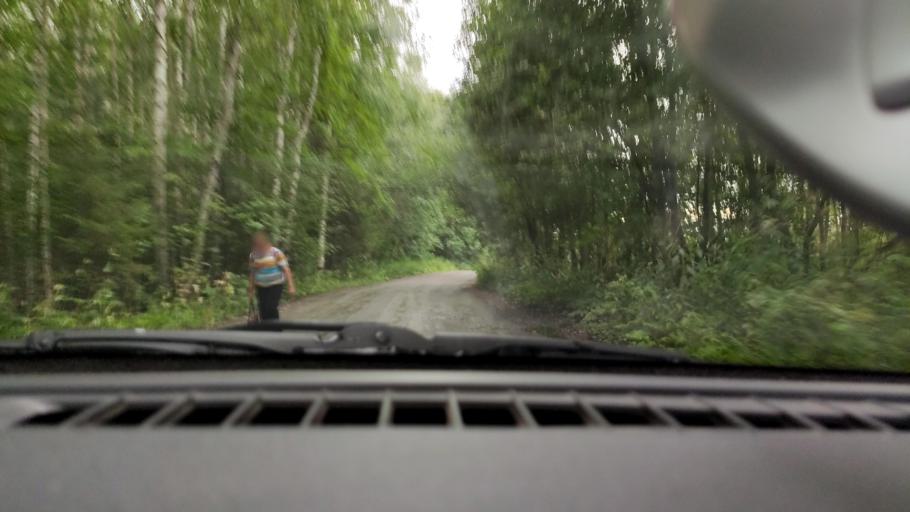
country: RU
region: Perm
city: Overyata
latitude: 58.0520
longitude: 55.9935
